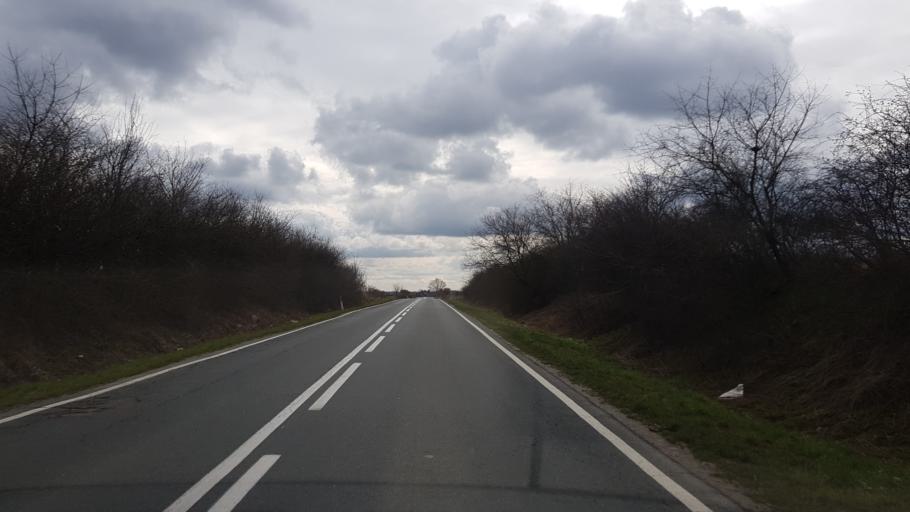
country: PL
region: West Pomeranian Voivodeship
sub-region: Powiat gryfinski
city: Banie
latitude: 53.1484
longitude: 14.6070
